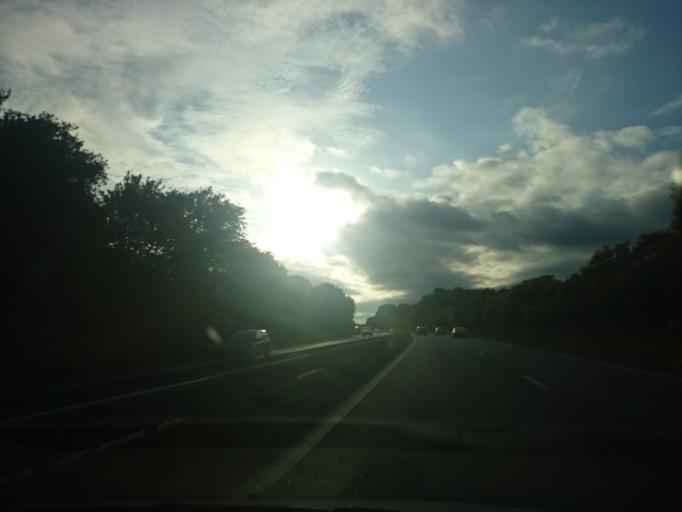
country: FR
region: Brittany
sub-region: Departement du Morbihan
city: Queven
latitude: 47.7766
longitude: -3.3953
